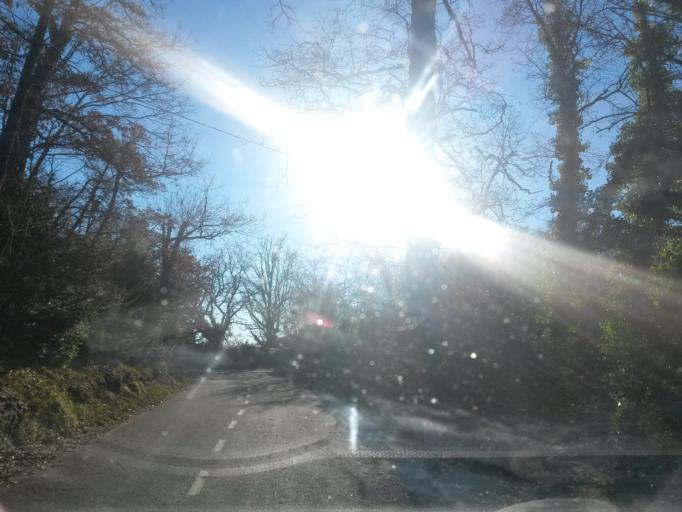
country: ES
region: Catalonia
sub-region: Provincia de Girona
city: les Planes d'Hostoles
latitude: 42.0230
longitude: 2.5359
